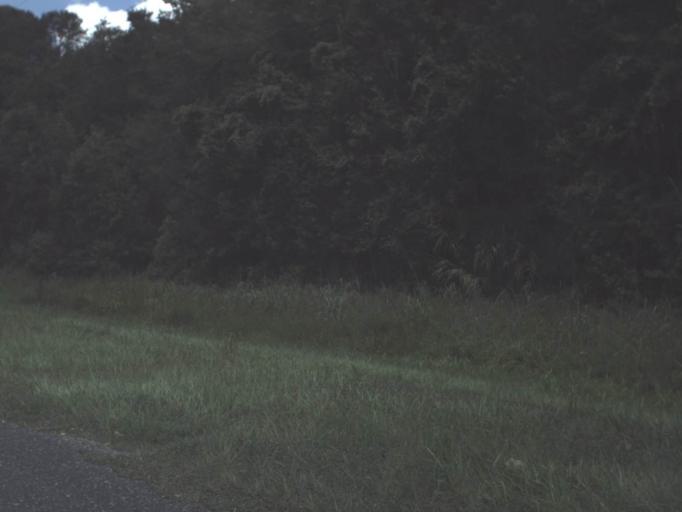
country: US
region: Florida
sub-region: Dixie County
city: Cross City
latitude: 29.6676
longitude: -83.2187
